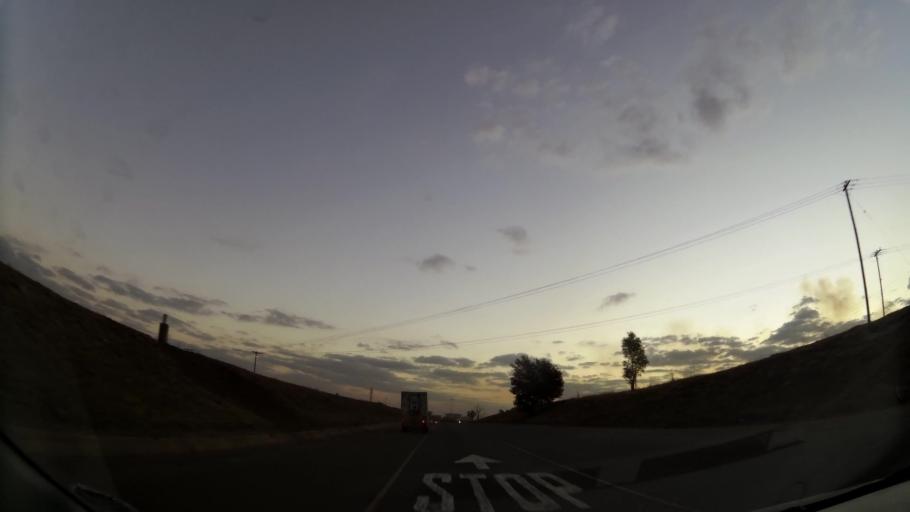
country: ZA
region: Gauteng
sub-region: West Rand District Municipality
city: Randfontein
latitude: -26.0742
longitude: 27.6514
